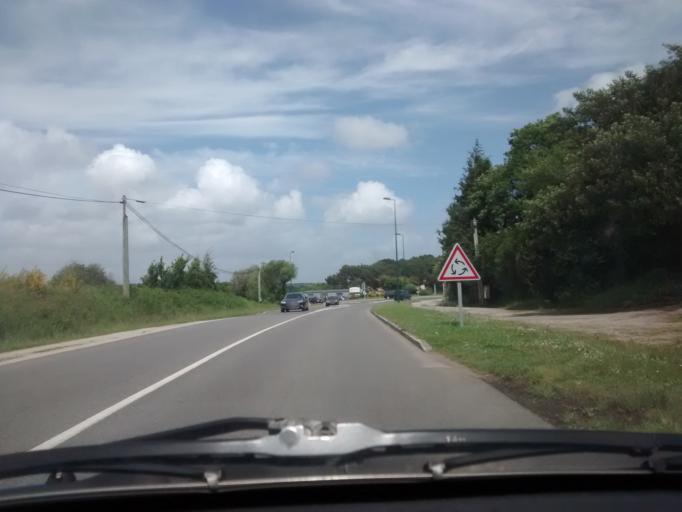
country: FR
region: Brittany
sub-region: Departement du Morbihan
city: Larmor-Baden
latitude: 47.6116
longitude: -2.8873
